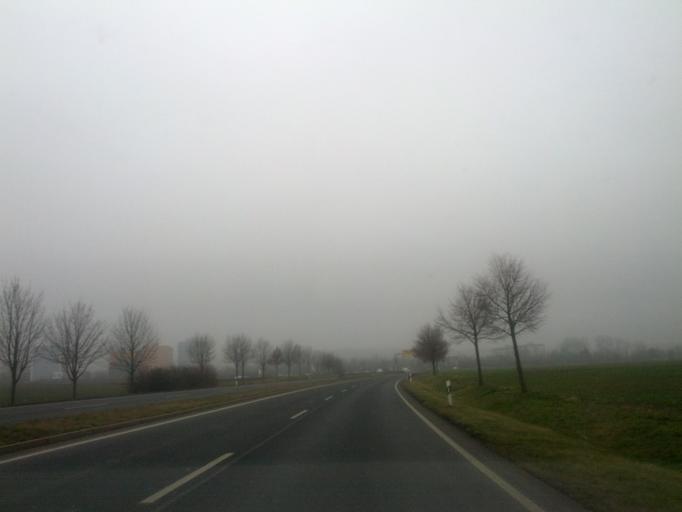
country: DE
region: Thuringia
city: Erfurt
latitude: 50.9584
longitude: 11.0856
